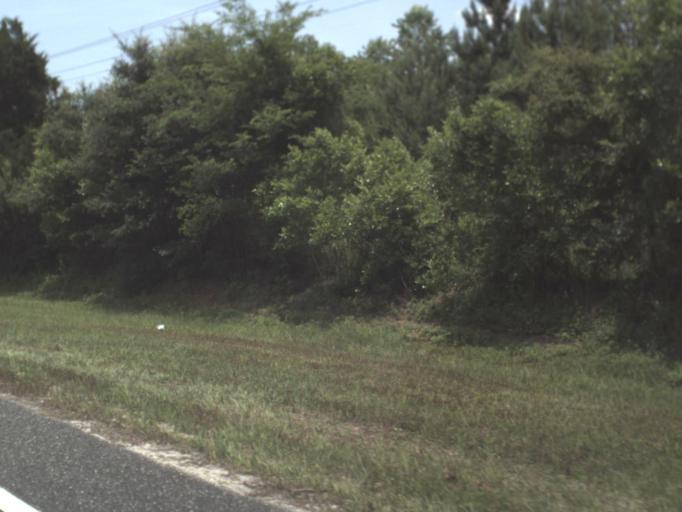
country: US
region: Florida
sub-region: Alachua County
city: Newberry
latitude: 29.6543
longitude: -82.5412
